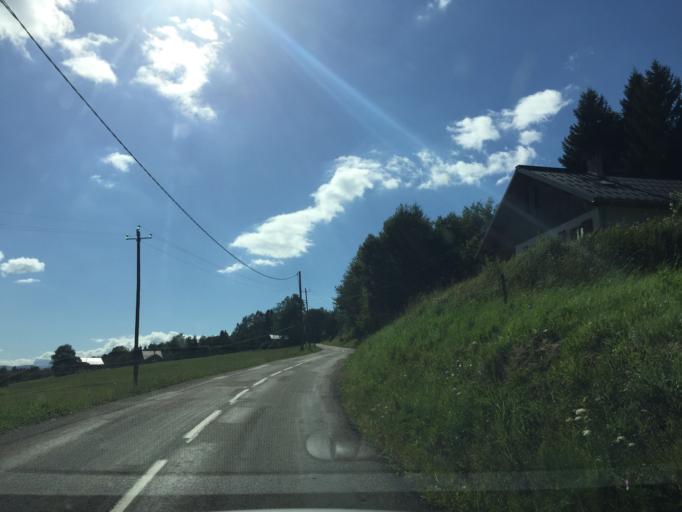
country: FR
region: Rhone-Alpes
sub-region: Departement de la Savoie
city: Coise-Saint-Jean-Pied-Gauthier
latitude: 45.4870
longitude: 6.2066
